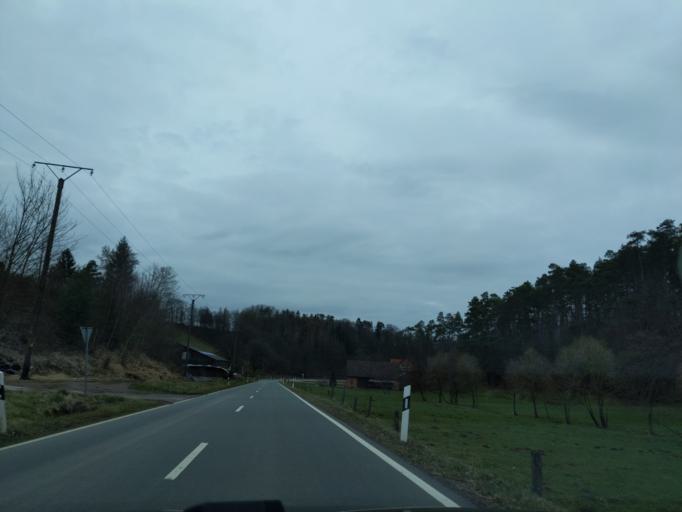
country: DE
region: Hesse
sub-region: Regierungsbezirk Kassel
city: Bad Arolsen
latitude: 51.3332
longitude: 9.0717
